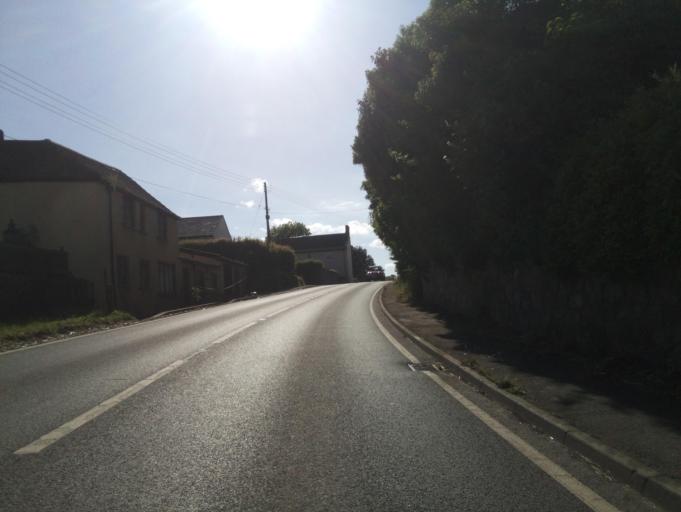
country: GB
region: England
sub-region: Somerset
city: Creech Saint Michael
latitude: 51.0479
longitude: -3.0019
